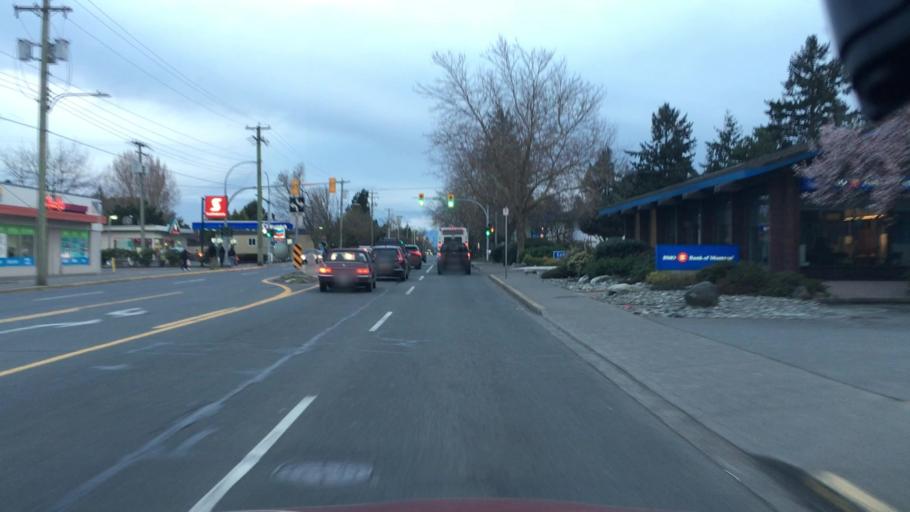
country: CA
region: British Columbia
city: Oak Bay
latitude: 48.4593
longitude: -123.3331
